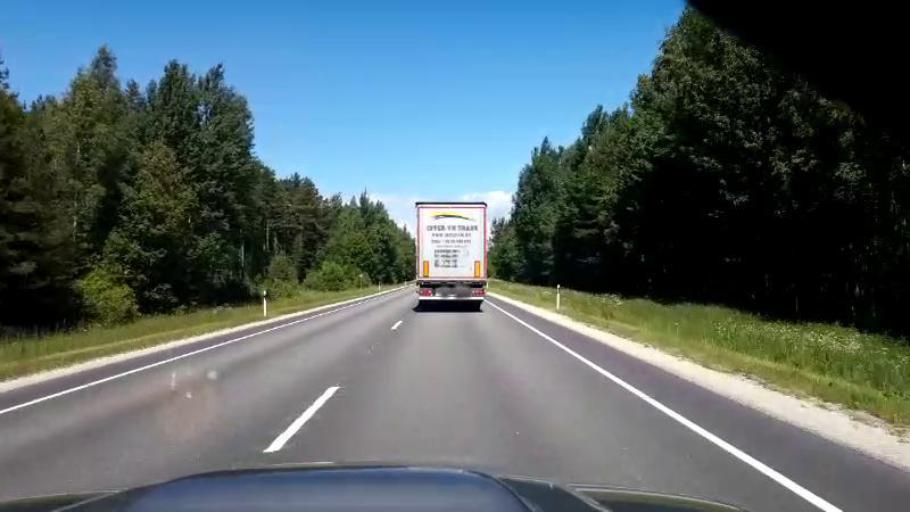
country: EE
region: Paernumaa
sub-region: Paernu linn
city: Parnu
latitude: 58.1193
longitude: 24.5110
